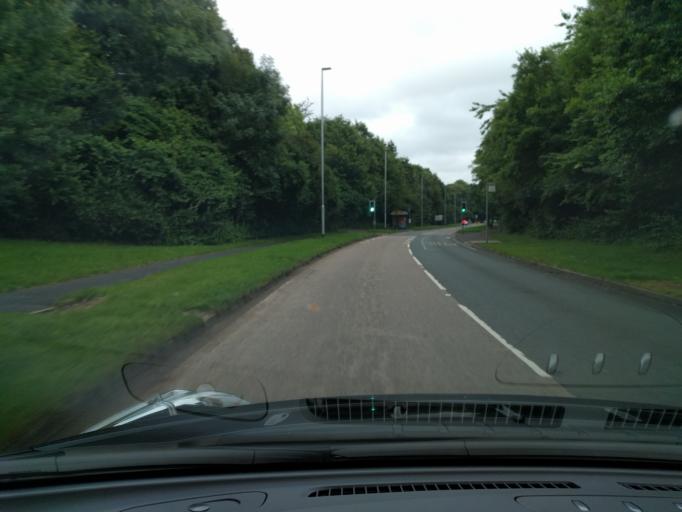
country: GB
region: England
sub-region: Warrington
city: Culcheth
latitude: 53.4269
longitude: -2.5079
